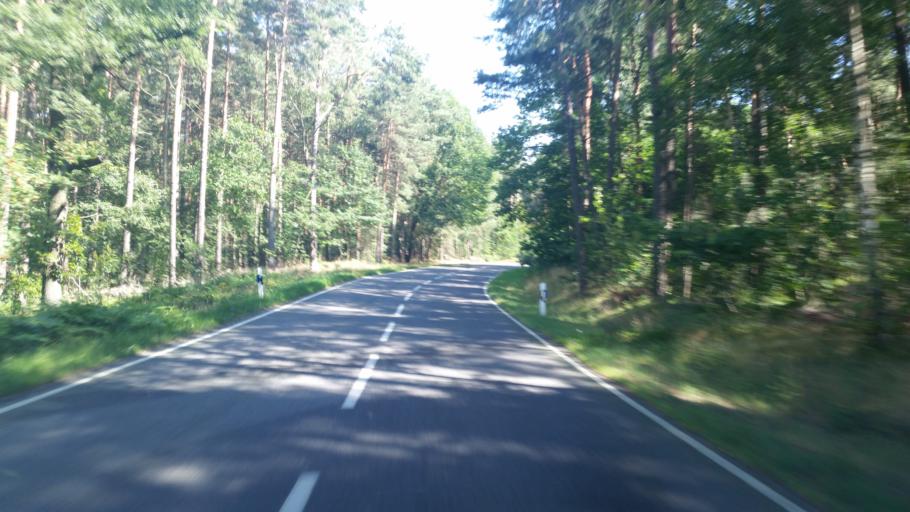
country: DE
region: Saxony
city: Neukirch
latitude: 51.3053
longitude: 14.0416
